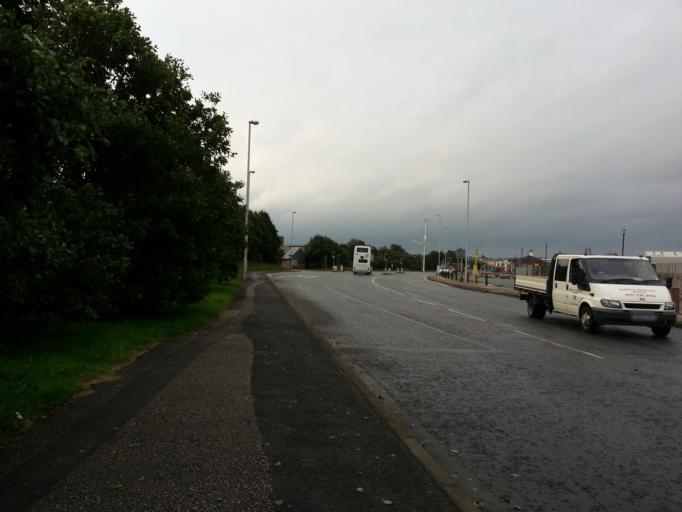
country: GB
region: England
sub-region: Metropolitan Borough of Wirral
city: Birkenhead
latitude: 53.4011
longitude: -3.0215
